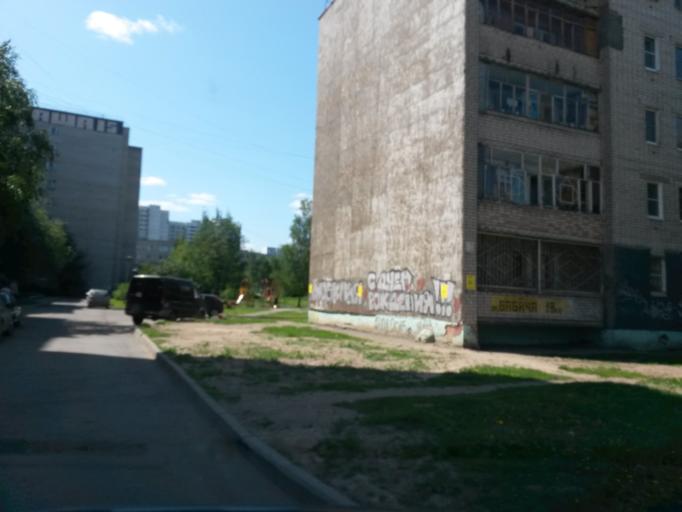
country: RU
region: Jaroslavl
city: Yaroslavl
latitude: 57.7013
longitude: 39.7693
